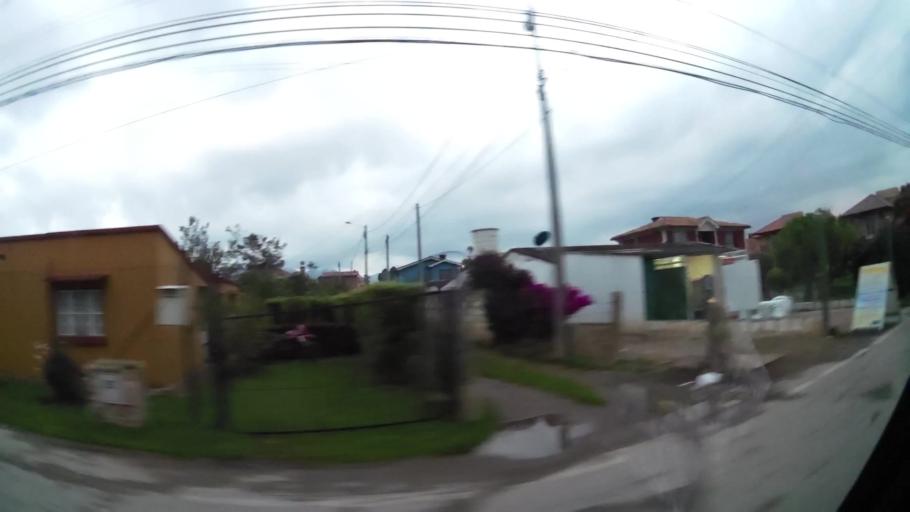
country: CO
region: Cundinamarca
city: Chia
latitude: 4.8406
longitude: -74.0711
